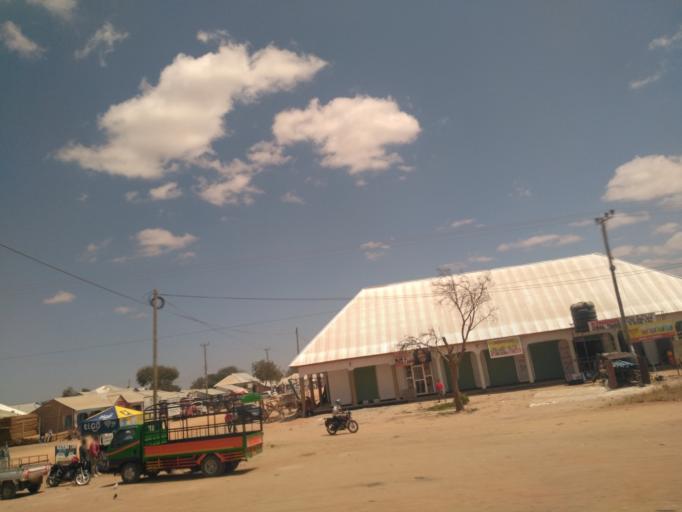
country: TZ
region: Dodoma
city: Kisasa
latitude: -6.1662
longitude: 35.7843
